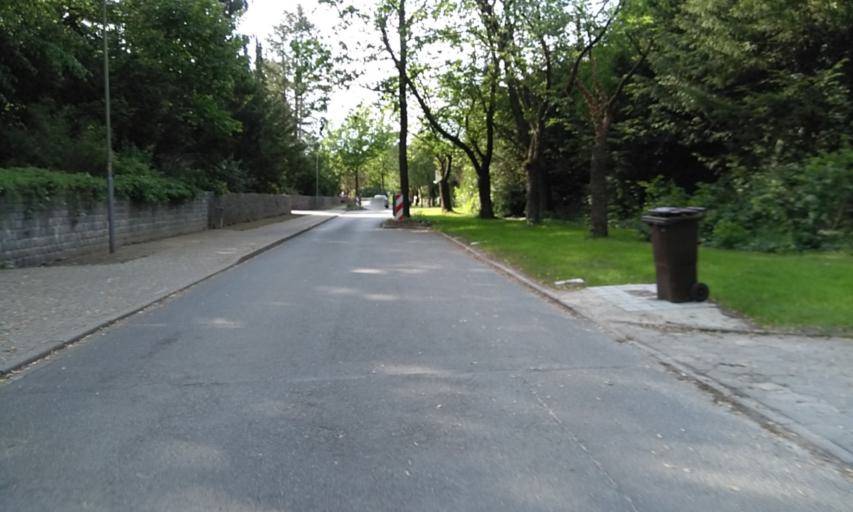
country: DE
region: Lower Saxony
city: Buxtehude
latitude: 53.4586
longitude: 9.7048
